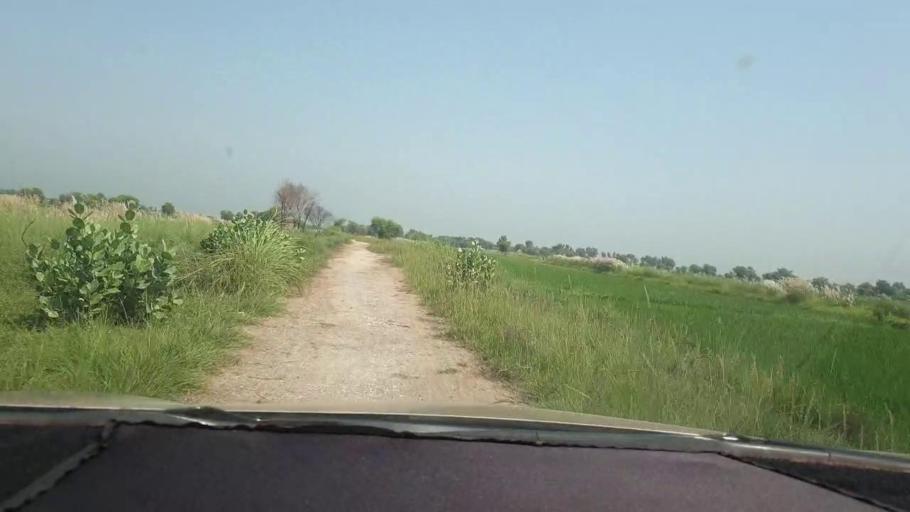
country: PK
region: Sindh
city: Kambar
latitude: 27.6038
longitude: 68.0640
